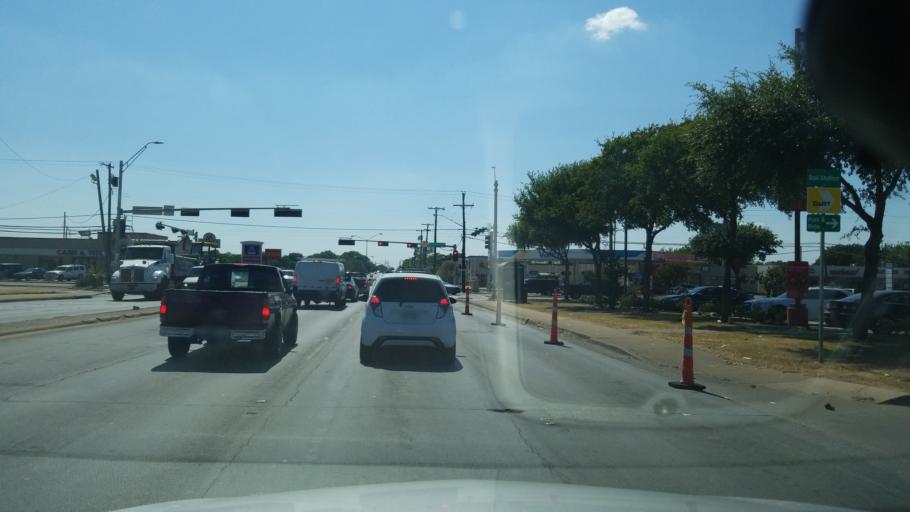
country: US
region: Texas
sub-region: Dallas County
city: Cockrell Hill
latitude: 32.7204
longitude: -96.8563
